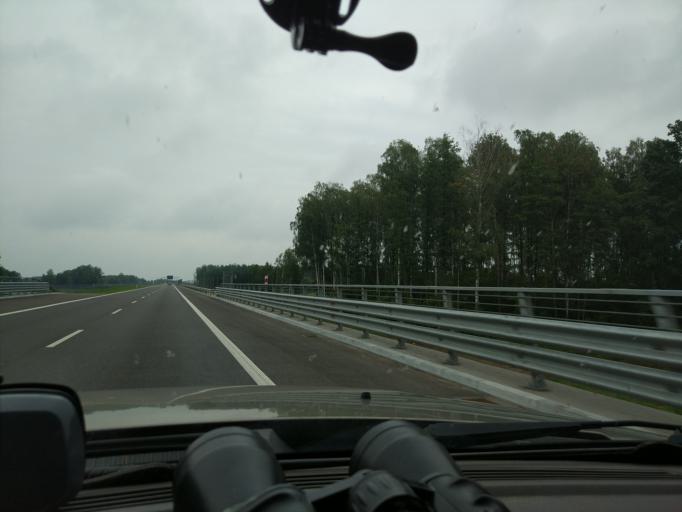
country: PL
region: Podlasie
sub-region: Powiat zambrowski
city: Szumowo
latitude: 52.9346
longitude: 22.1406
